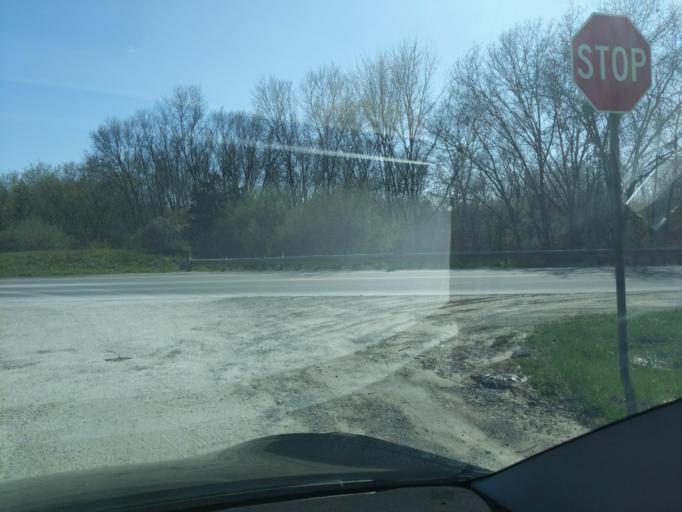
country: US
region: Michigan
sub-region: Washtenaw County
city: Chelsea
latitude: 42.3833
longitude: -84.0838
